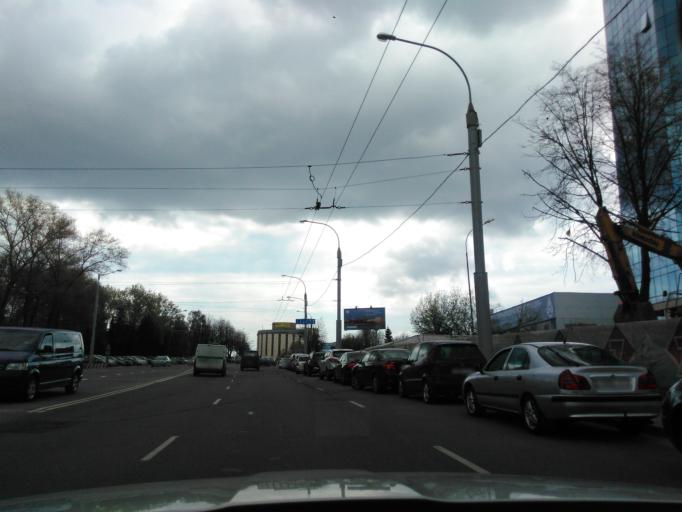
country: BY
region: Minsk
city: Minsk
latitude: 53.9049
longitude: 27.5334
